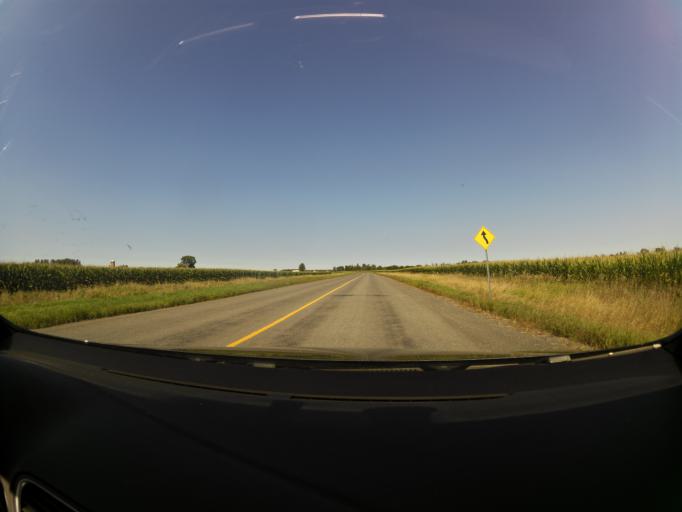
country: CA
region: Ontario
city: Arnprior
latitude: 45.3690
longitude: -76.3414
